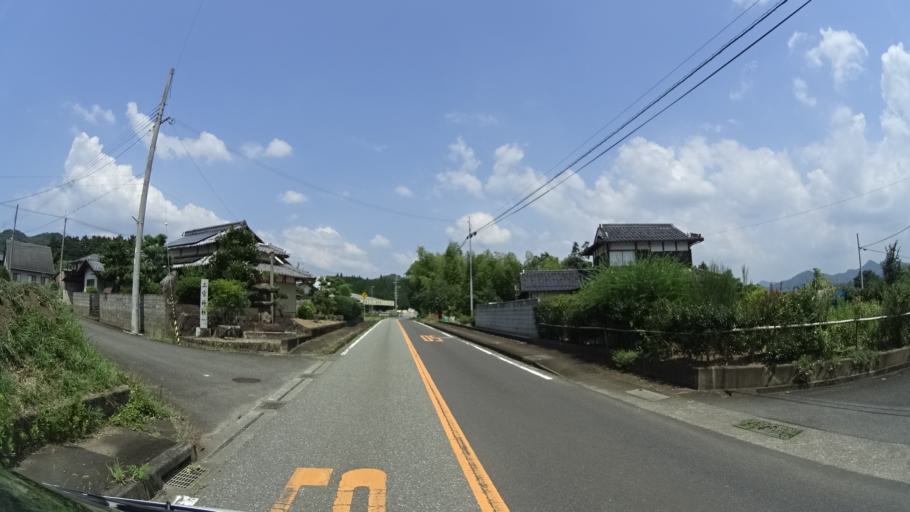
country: JP
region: Kyoto
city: Fukuchiyama
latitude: 35.2511
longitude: 135.1447
